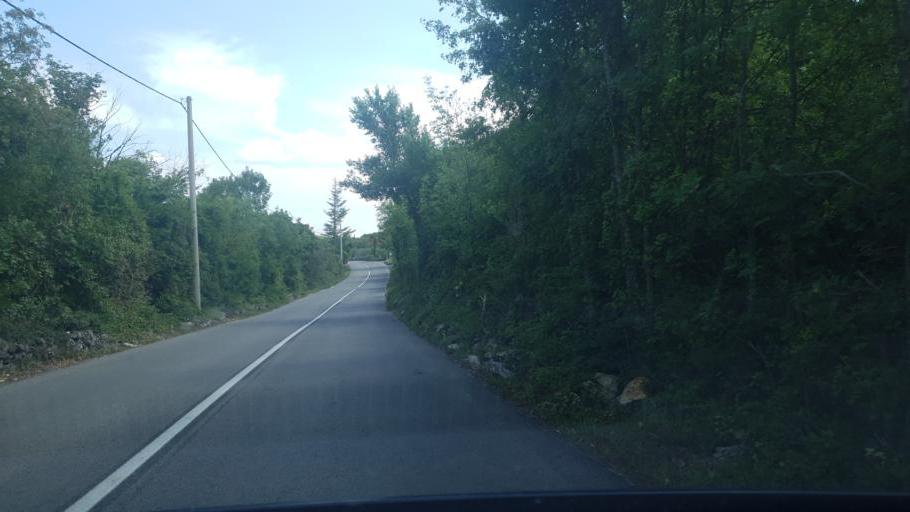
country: HR
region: Primorsko-Goranska
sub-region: Grad Crikvenica
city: Crikvenica
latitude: 45.1225
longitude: 14.6262
